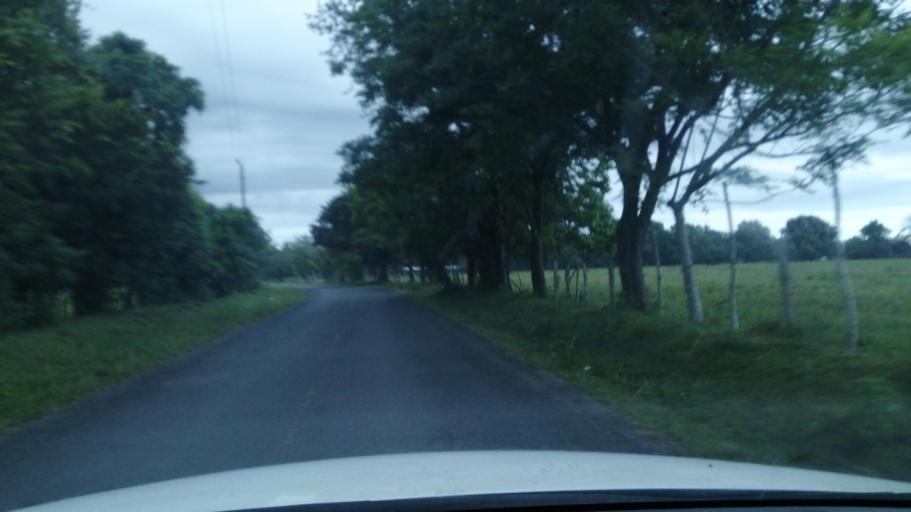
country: PA
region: Chiriqui
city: Alanje
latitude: 8.4048
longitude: -82.5003
